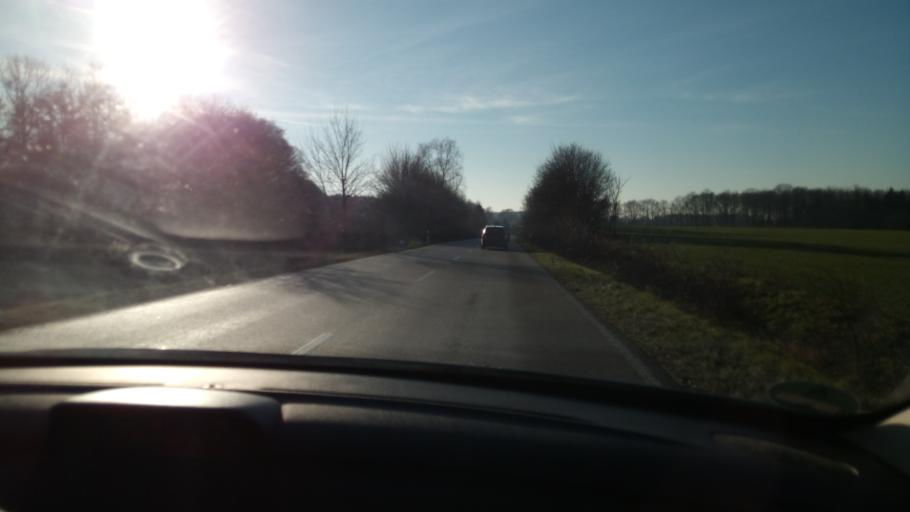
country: DE
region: Schleswig-Holstein
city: Basedow
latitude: 53.4101
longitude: 10.5655
